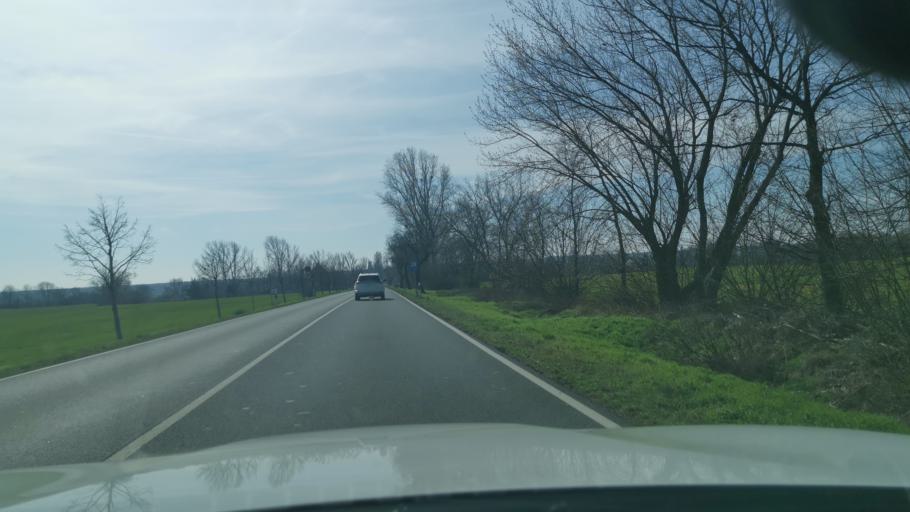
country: DE
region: Saxony-Anhalt
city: Kemberg
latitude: 51.7815
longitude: 12.6481
